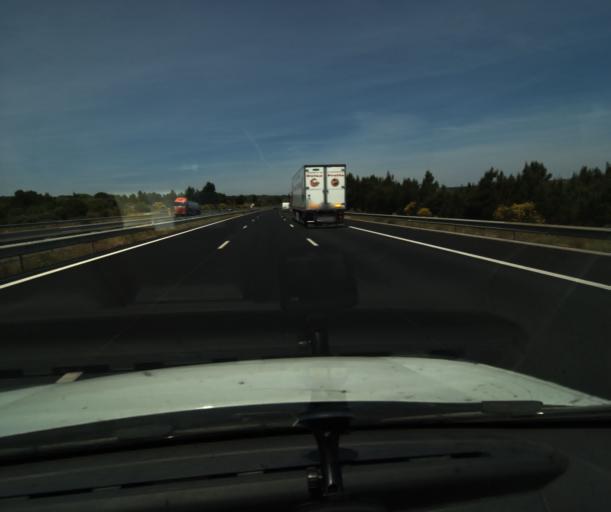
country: FR
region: Languedoc-Roussillon
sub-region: Departement de l'Aude
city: Sigean
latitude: 42.9638
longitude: 2.9689
